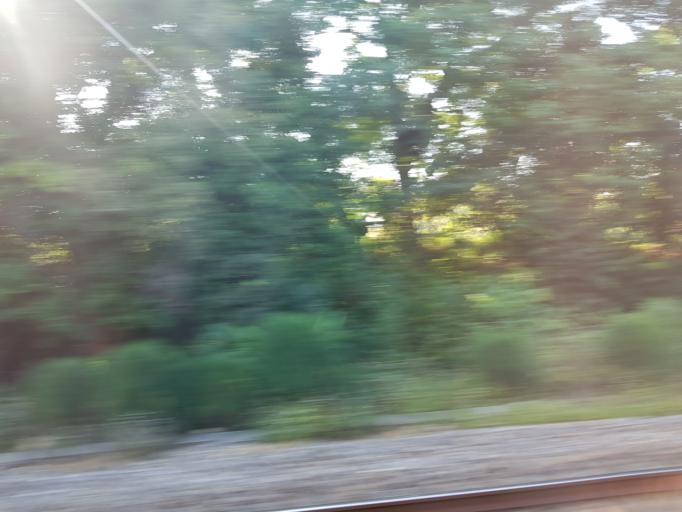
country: TW
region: Taiwan
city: Fengyuan
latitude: 24.2960
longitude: 120.7326
